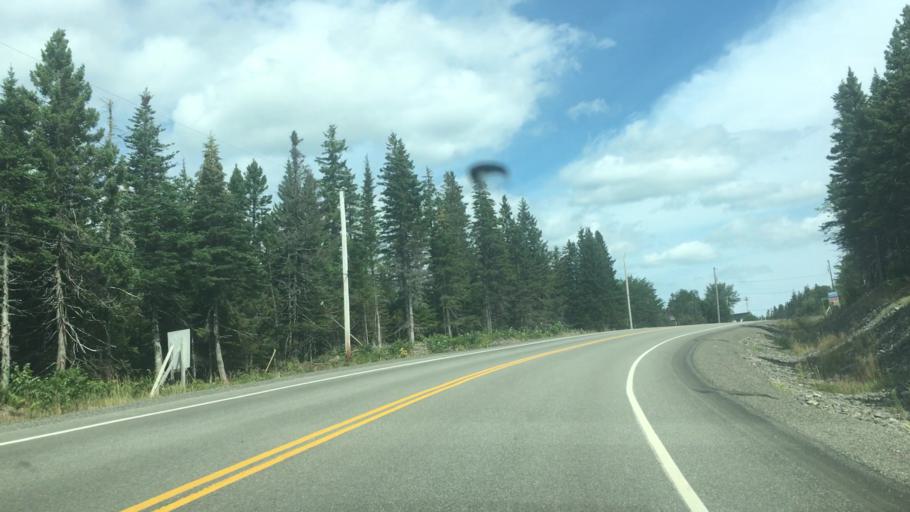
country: CA
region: Nova Scotia
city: Sydney Mines
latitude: 46.3269
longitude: -60.6059
